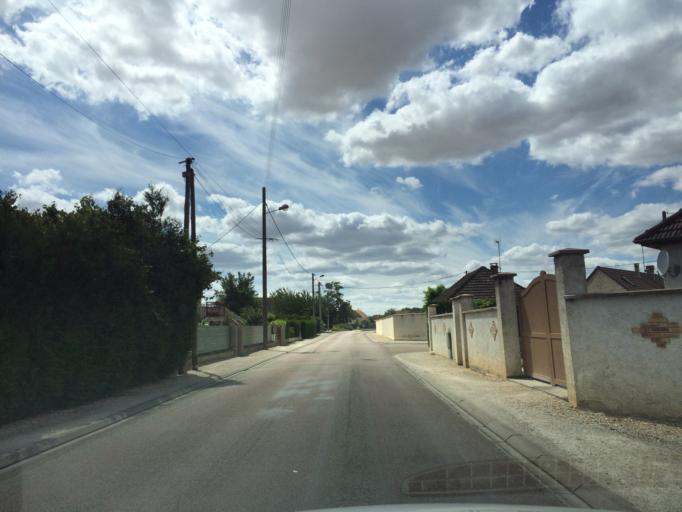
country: FR
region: Bourgogne
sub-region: Departement de l'Yonne
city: Laroche-Saint-Cydroine
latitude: 47.9509
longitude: 3.4804
